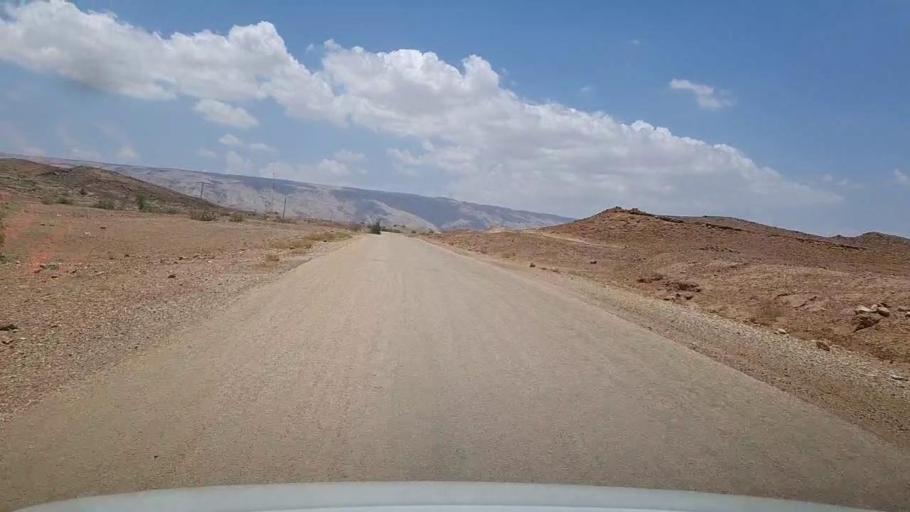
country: PK
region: Sindh
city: Bhan
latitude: 26.3184
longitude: 67.5595
